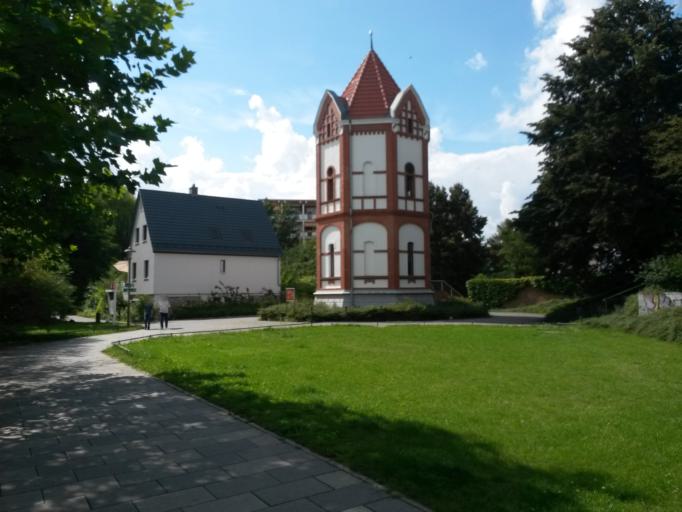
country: DE
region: Brandenburg
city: Schwedt (Oder)
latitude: 53.0531
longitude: 14.2871
